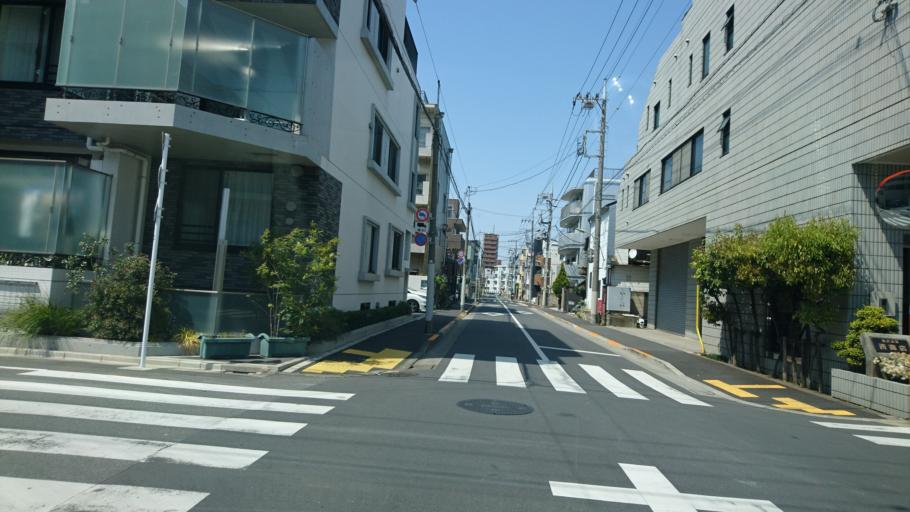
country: JP
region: Kanagawa
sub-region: Kawasaki-shi
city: Kawasaki
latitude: 35.5689
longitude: 139.7058
